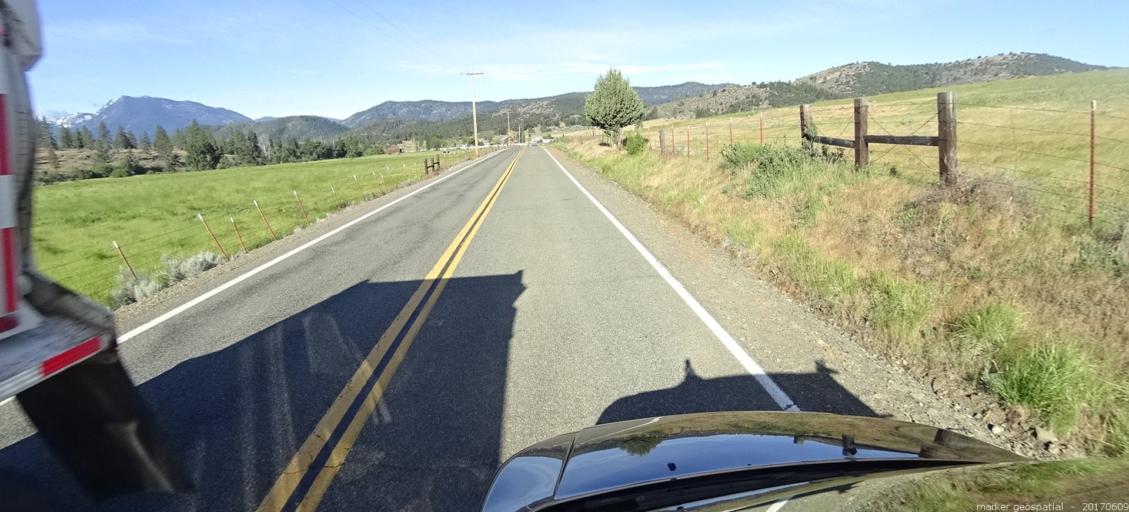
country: US
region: California
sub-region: Siskiyou County
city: Weed
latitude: 41.3731
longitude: -122.7055
